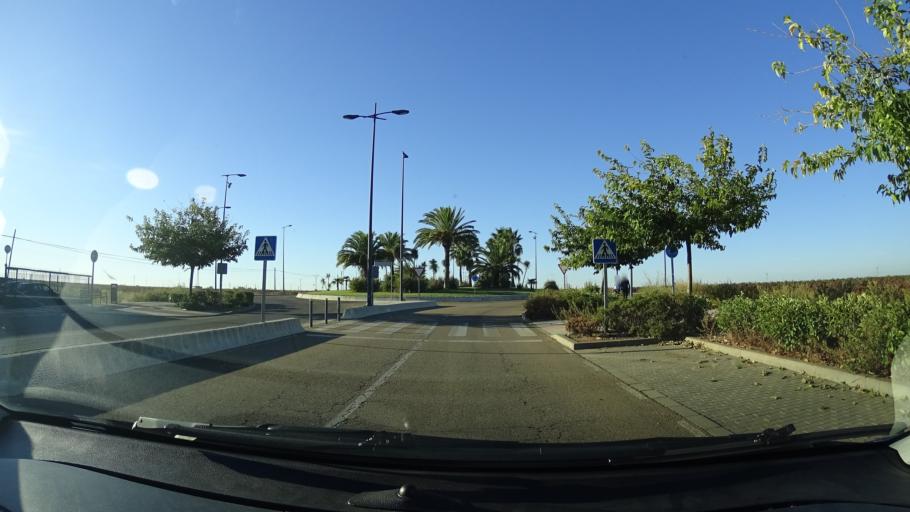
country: ES
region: Extremadura
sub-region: Provincia de Badajoz
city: Almendralejo
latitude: 38.7051
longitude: -6.4012
